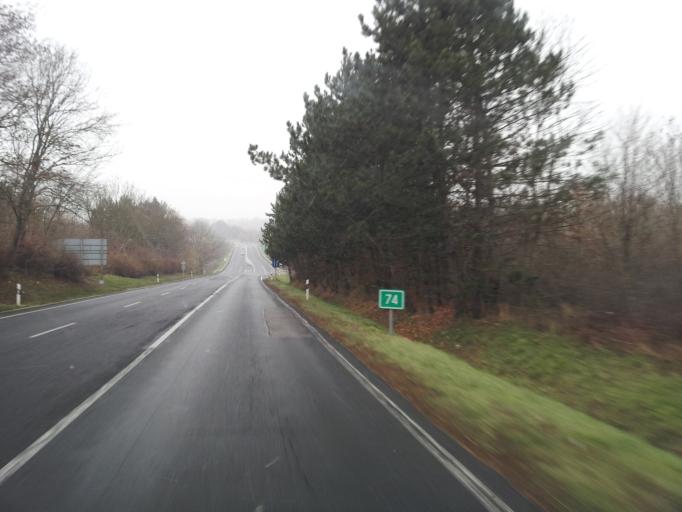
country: HU
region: Veszprem
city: Urkut
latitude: 47.1507
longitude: 17.6620
